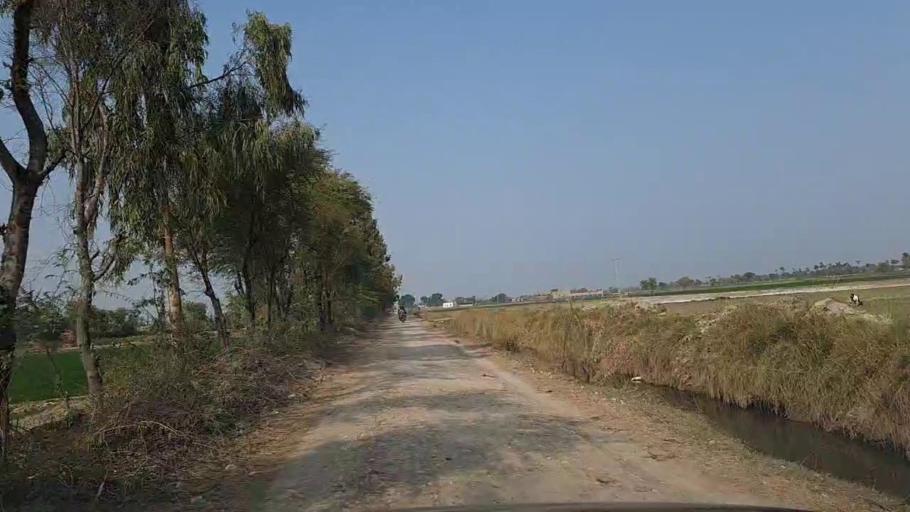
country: PK
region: Sindh
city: Daur
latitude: 26.3929
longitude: 68.4237
